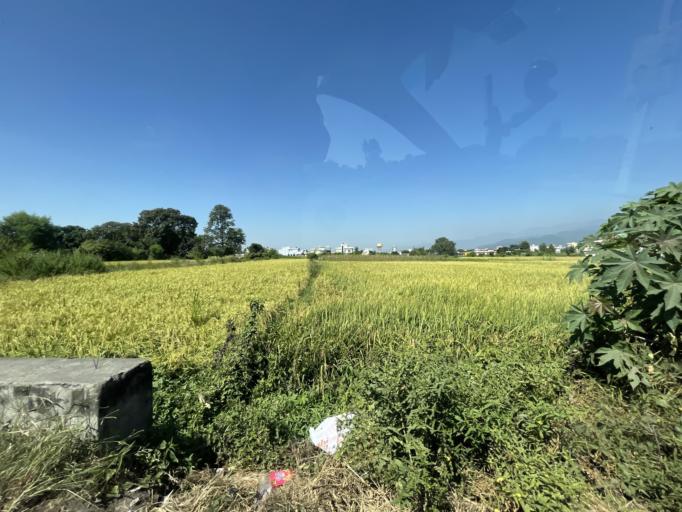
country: IN
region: Uttarakhand
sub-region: Naini Tal
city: Haldwani
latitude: 29.2091
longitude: 79.4940
